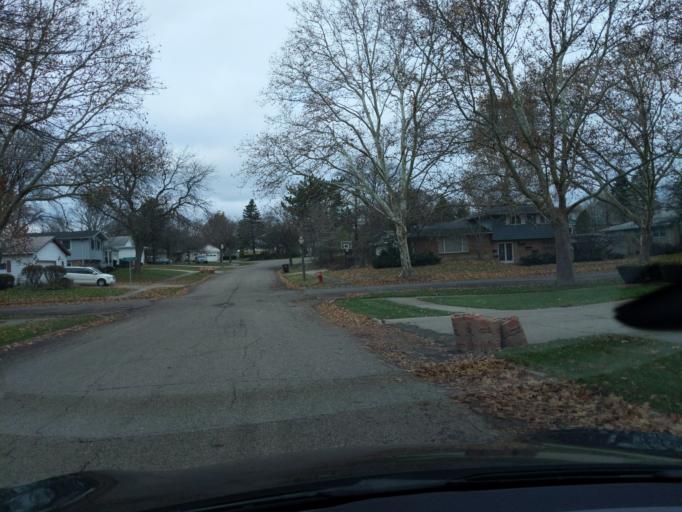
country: US
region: Michigan
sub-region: Ingham County
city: Edgemont Park
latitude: 42.7092
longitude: -84.5861
